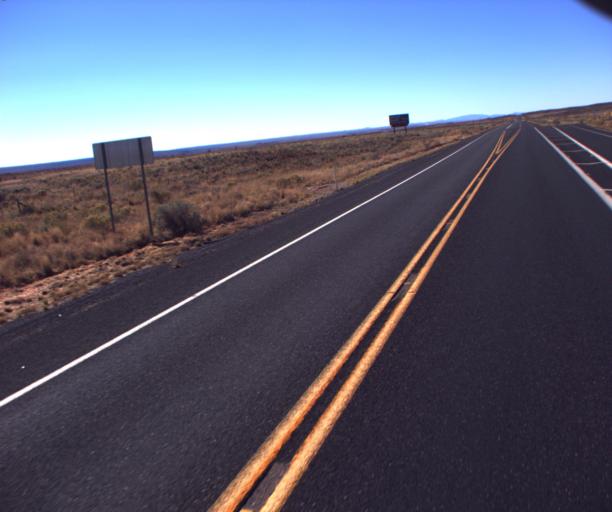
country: US
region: Arizona
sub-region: Coconino County
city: Fredonia
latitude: 36.9325
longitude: -112.5584
